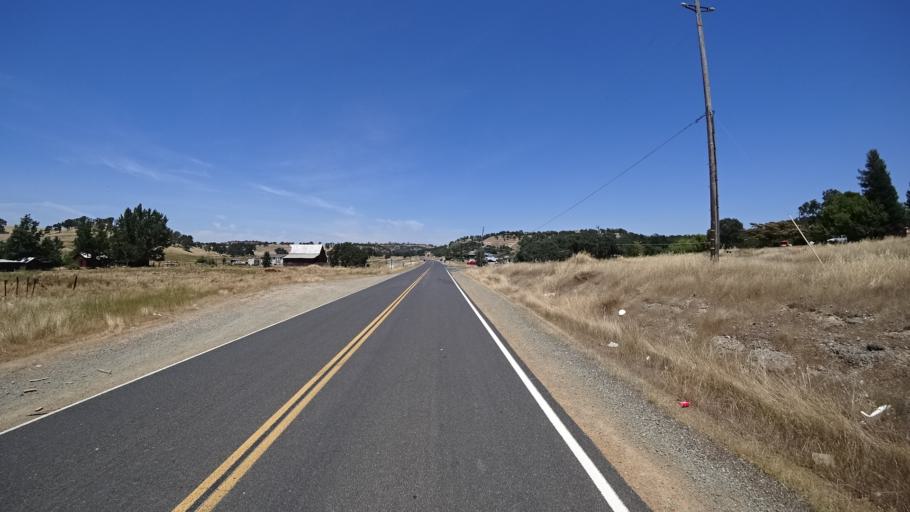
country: US
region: California
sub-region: Calaveras County
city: Rancho Calaveras
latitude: 38.1103
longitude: -120.8794
